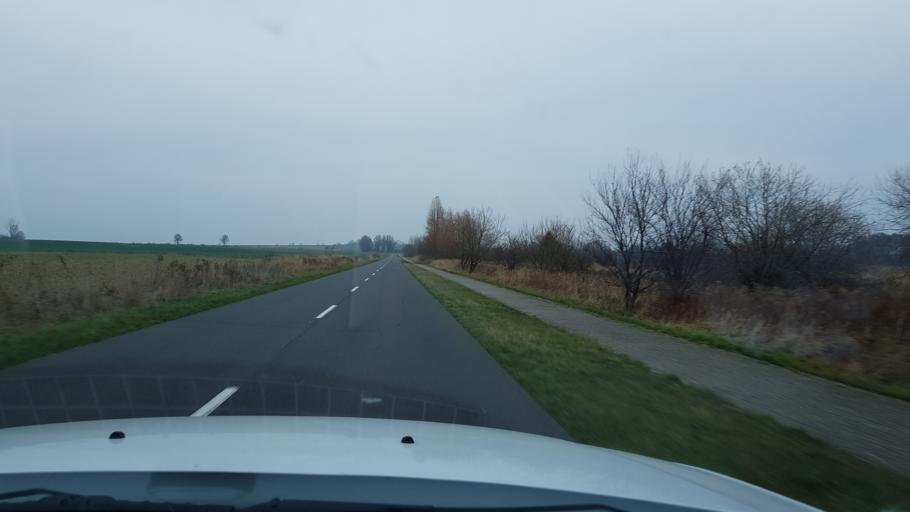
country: PL
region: West Pomeranian Voivodeship
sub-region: Powiat kamienski
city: Kamien Pomorski
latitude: 53.9681
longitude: 14.6879
